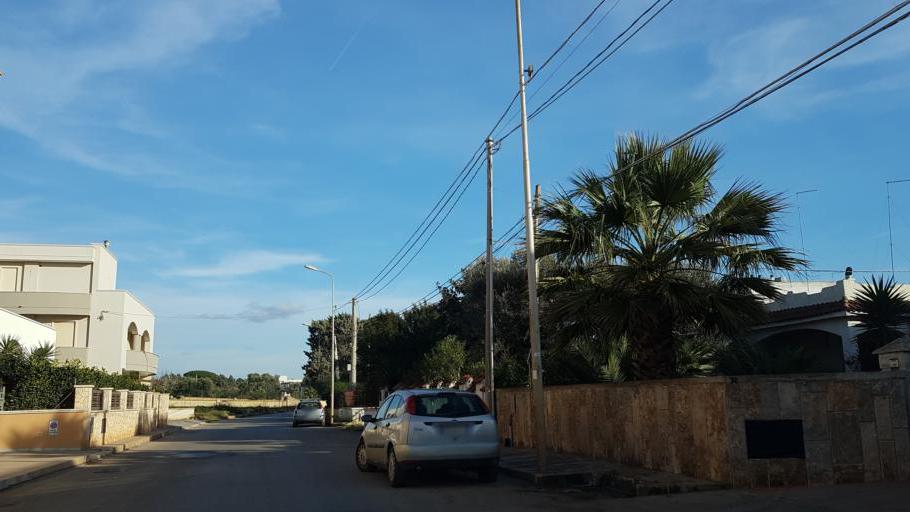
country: IT
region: Apulia
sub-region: Provincia di Brindisi
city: Carovigno
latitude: 40.7026
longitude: 17.6679
